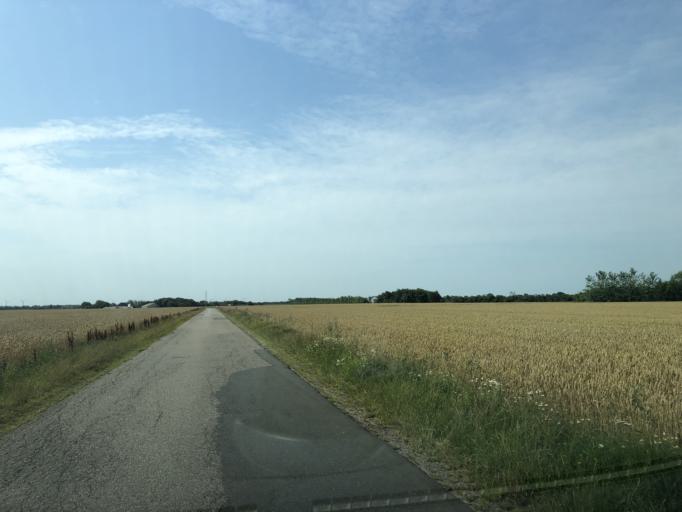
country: DK
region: Central Jutland
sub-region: Lemvig Kommune
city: Lemvig
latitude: 56.4460
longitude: 8.2918
